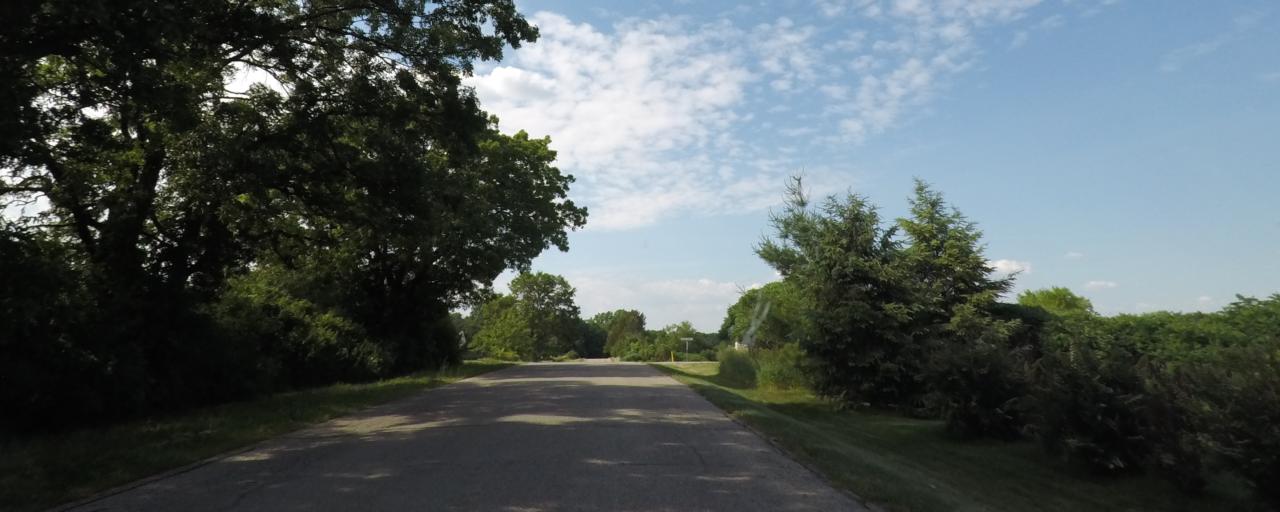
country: US
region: Wisconsin
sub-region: Walworth County
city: Elkhorn
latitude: 42.7724
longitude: -88.5438
